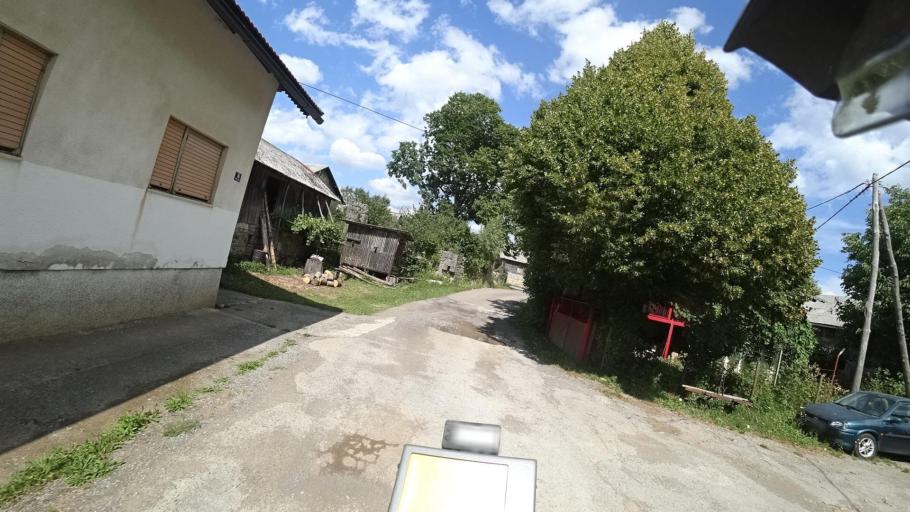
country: HR
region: Licko-Senjska
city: Brinje
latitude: 45.1168
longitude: 15.0915
